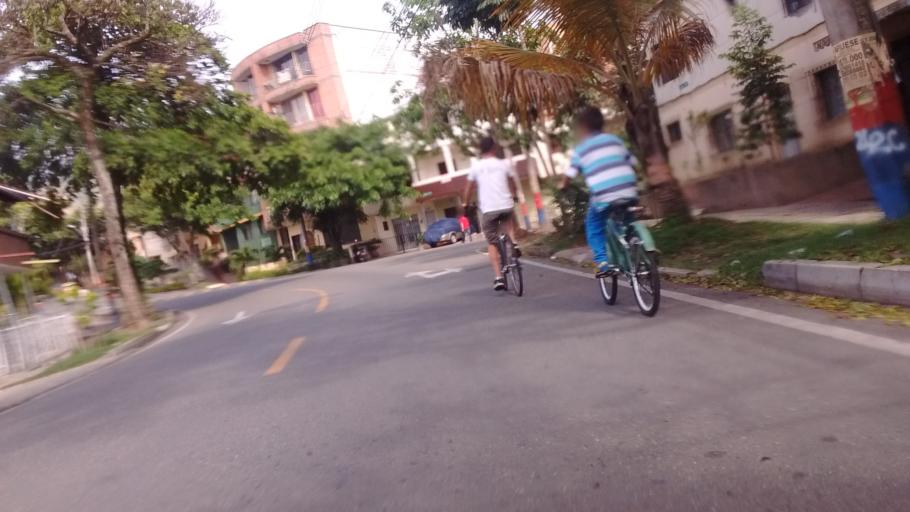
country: CO
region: Antioquia
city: Medellin
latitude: 6.2548
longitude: -75.6170
